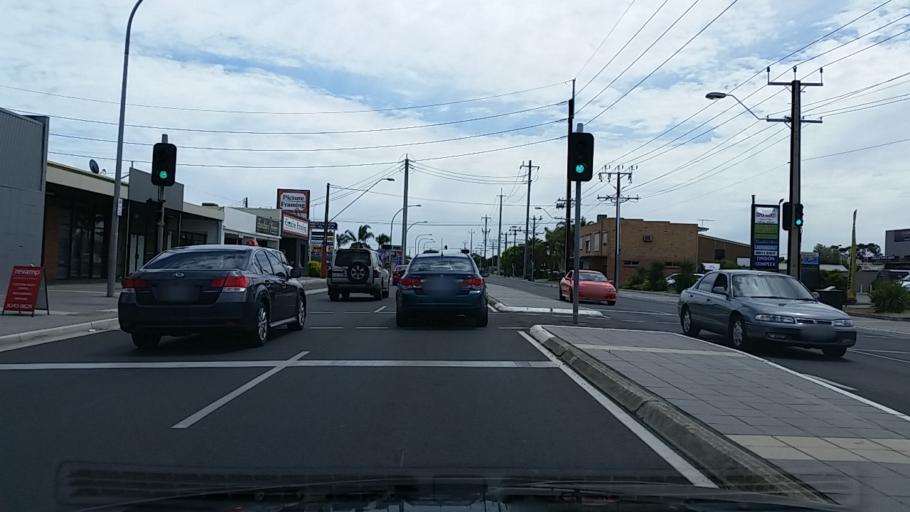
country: AU
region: South Australia
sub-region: Charles Sturt
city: Woodville West
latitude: -34.8930
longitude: 138.5317
